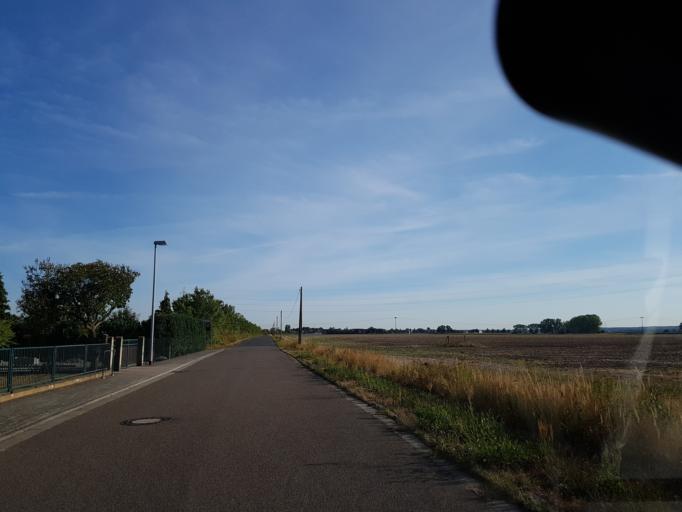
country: DE
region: Saxony
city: Nauwalde
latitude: 51.4485
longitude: 13.4196
